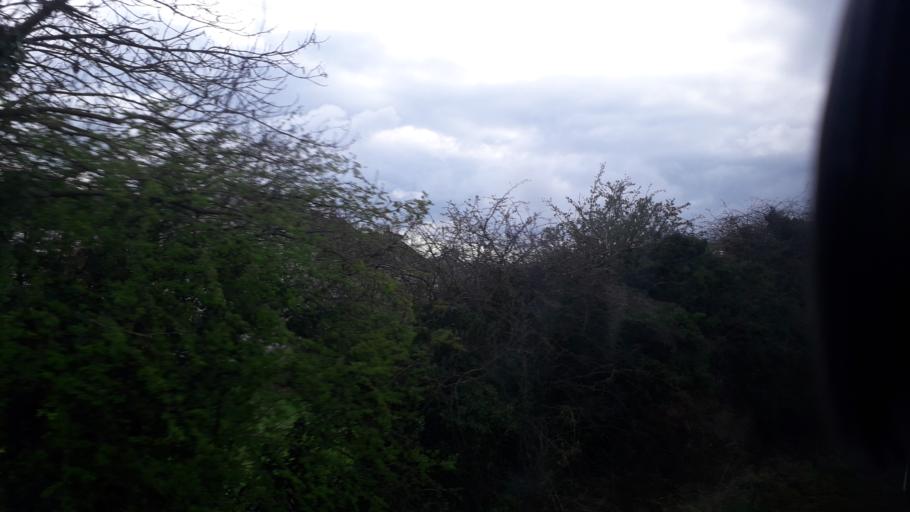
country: IE
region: Leinster
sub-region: An Longfort
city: Longford
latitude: 53.7265
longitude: -7.7812
